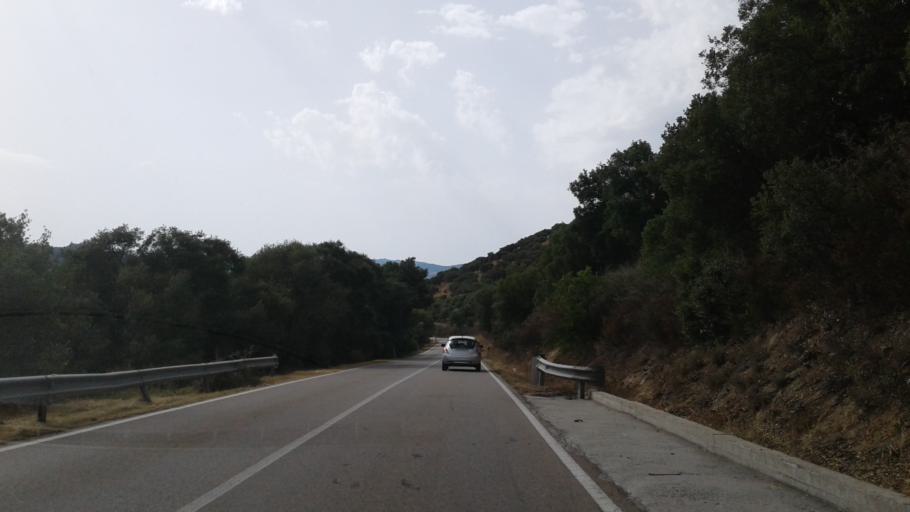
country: IT
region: Sardinia
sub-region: Provincia di Olbia-Tempio
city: Sant'Antonio di Gallura
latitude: 40.9605
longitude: 9.2909
